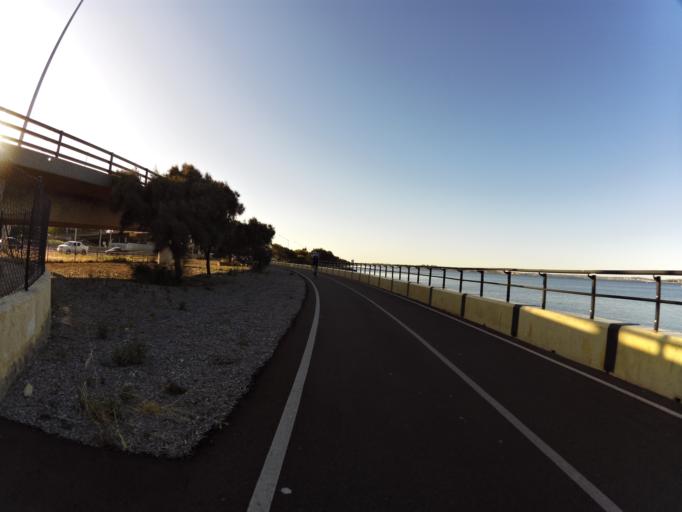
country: AU
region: Western Australia
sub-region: South Perth
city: South Perth
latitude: -31.9722
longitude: 115.8470
